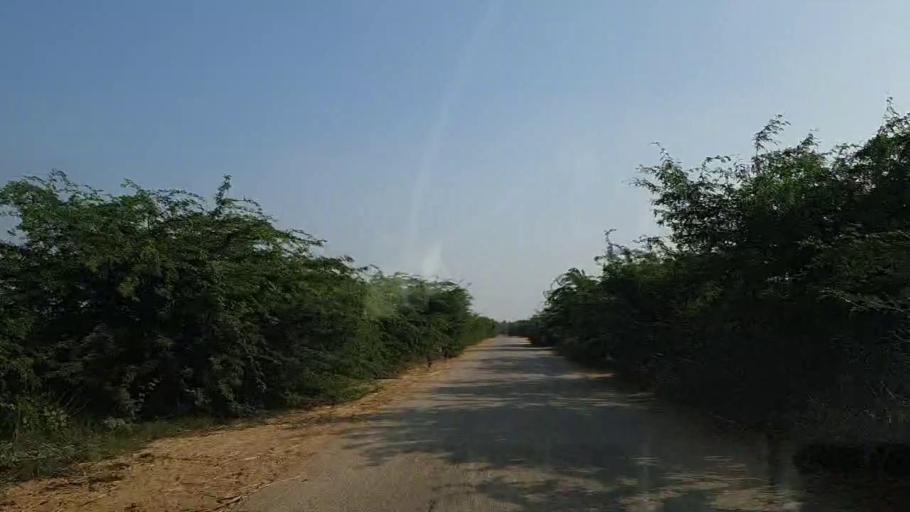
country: PK
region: Sindh
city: Mirpur Sakro
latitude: 24.6219
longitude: 67.6580
